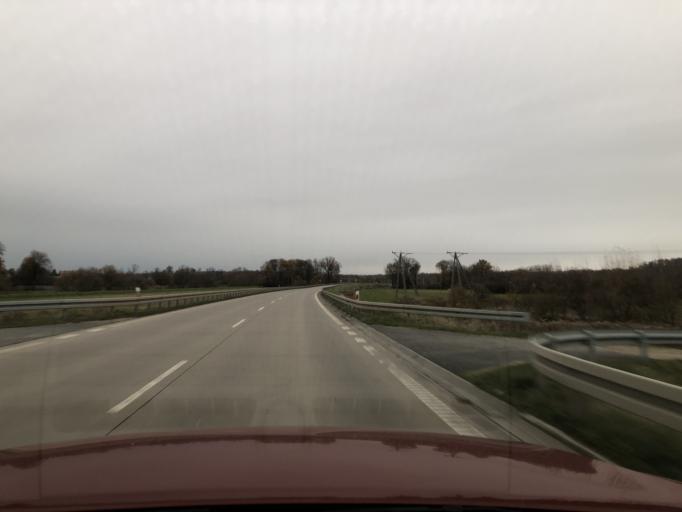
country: PL
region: Lower Silesian Voivodeship
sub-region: Powiat swidnicki
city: Zarow
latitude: 50.9496
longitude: 16.4843
